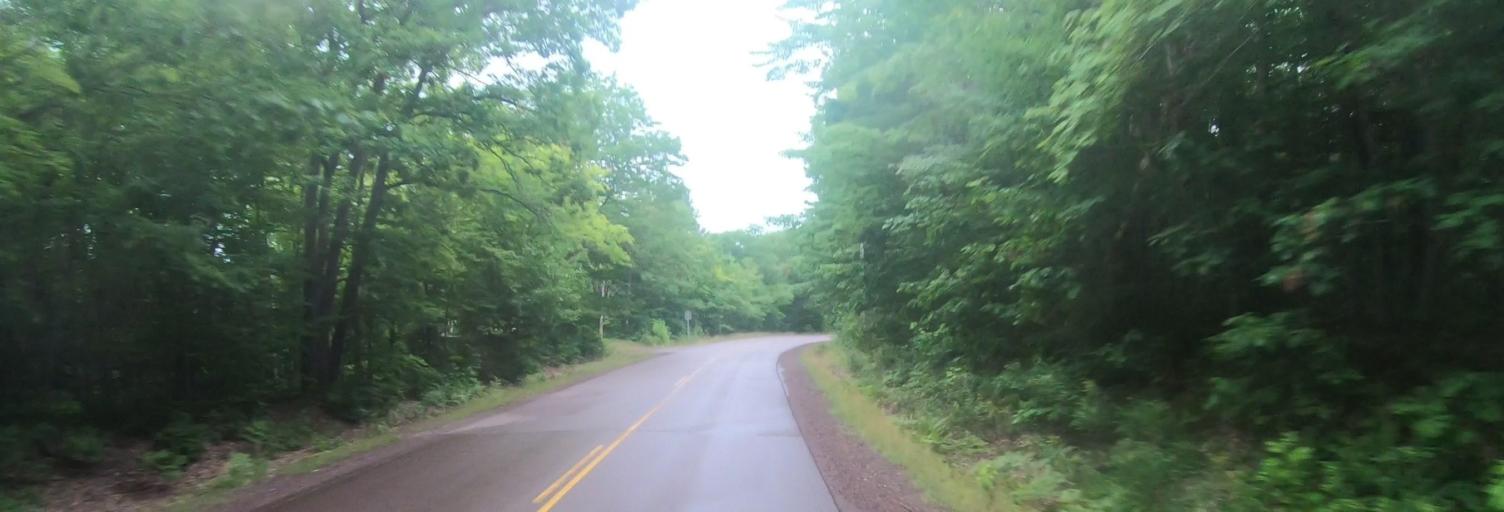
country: US
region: Michigan
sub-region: Keweenaw County
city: Eagle River
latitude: 47.2960
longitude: -88.3281
